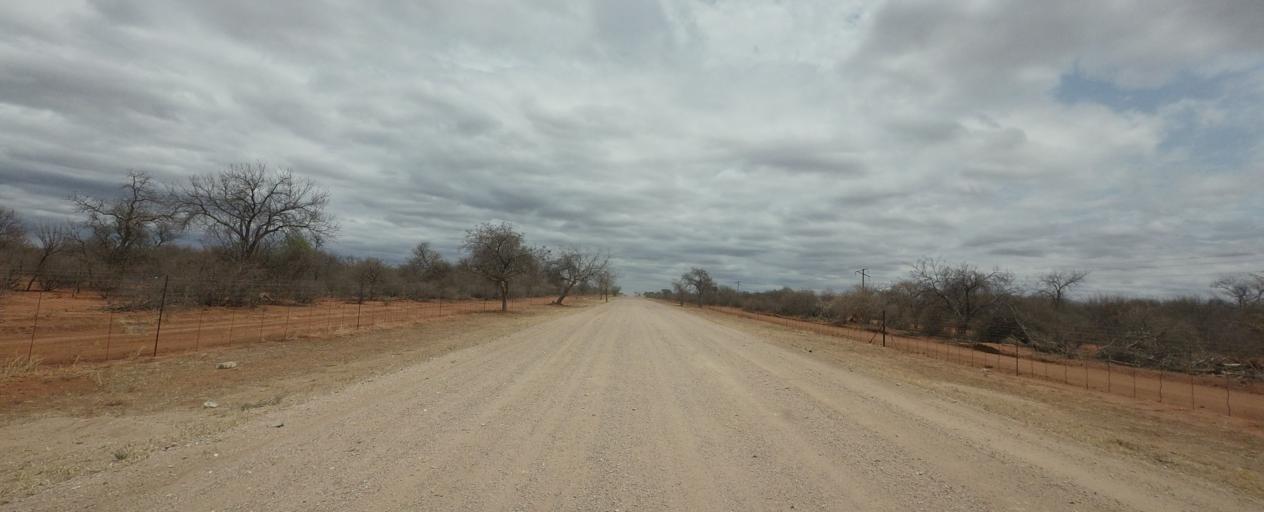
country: BW
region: Central
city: Mathathane
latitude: -22.6879
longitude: 28.6442
